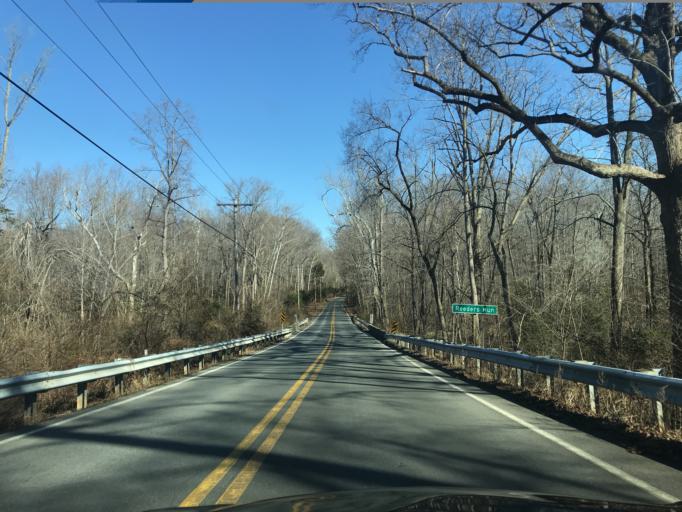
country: US
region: Virginia
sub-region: Prince William County
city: Cherry Hill
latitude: 38.5324
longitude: -77.2280
